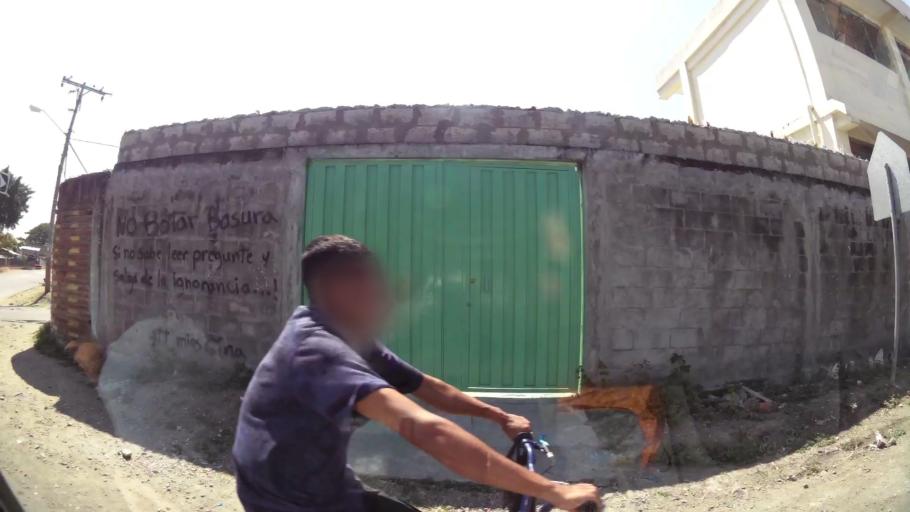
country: EC
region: Guayas
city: Guayaquil
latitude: -2.1286
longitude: -79.9245
